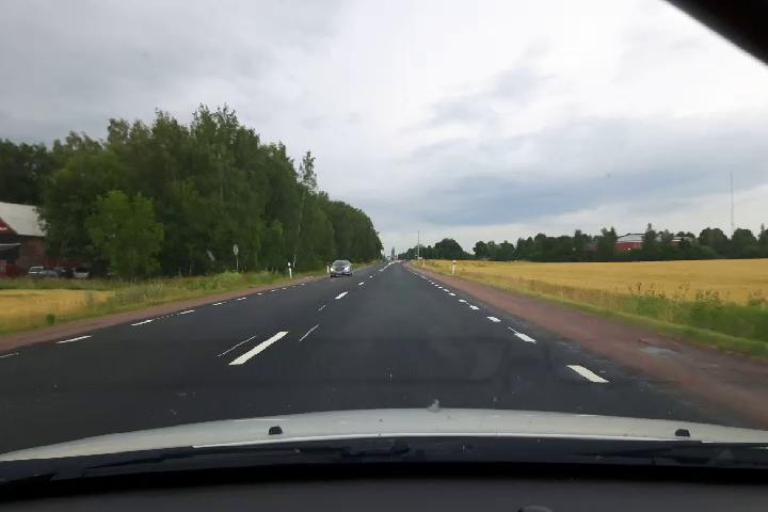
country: SE
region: Uppsala
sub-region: Uppsala Kommun
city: Gamla Uppsala
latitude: 59.8853
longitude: 17.6194
